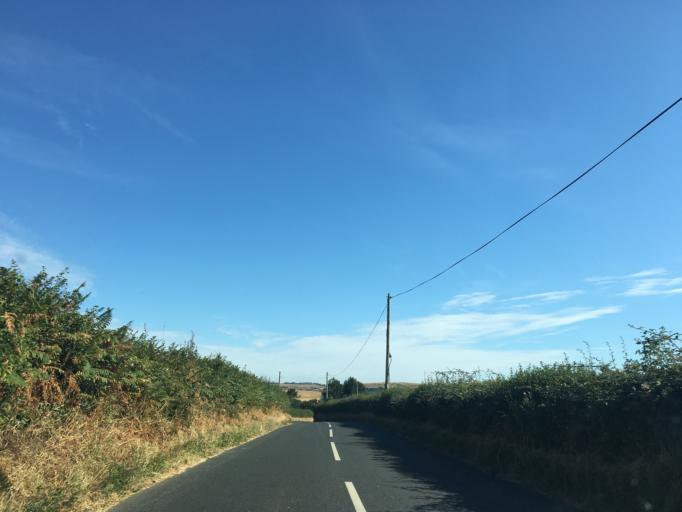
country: GB
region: England
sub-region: Isle of Wight
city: Chale
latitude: 50.6255
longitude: -1.3207
